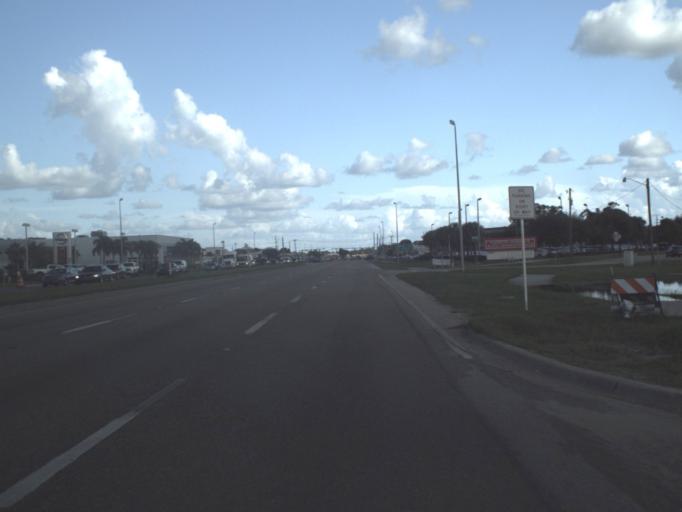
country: US
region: Florida
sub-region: Charlotte County
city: Port Charlotte
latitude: 26.9676
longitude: -82.0790
